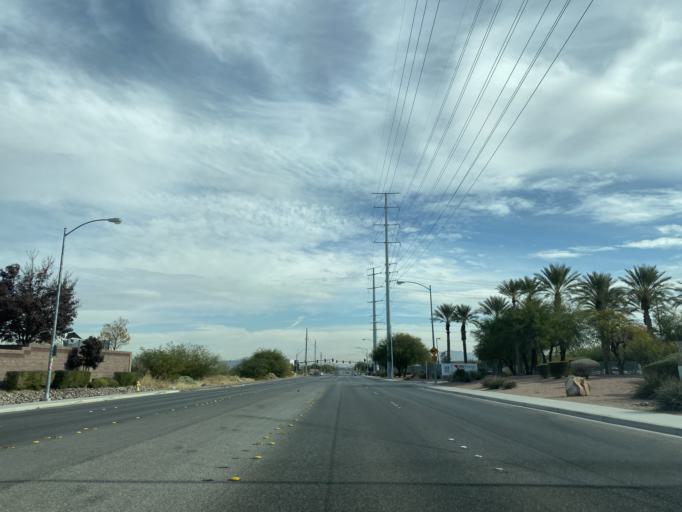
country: US
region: Nevada
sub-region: Clark County
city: North Las Vegas
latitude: 36.2469
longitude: -115.1198
